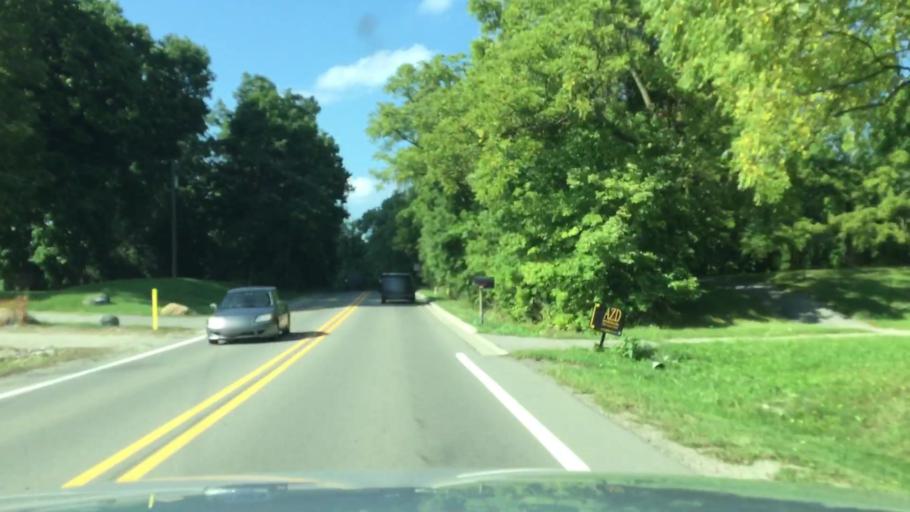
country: US
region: Michigan
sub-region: Oakland County
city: West Bloomfield Township
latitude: 42.5819
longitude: -83.4118
